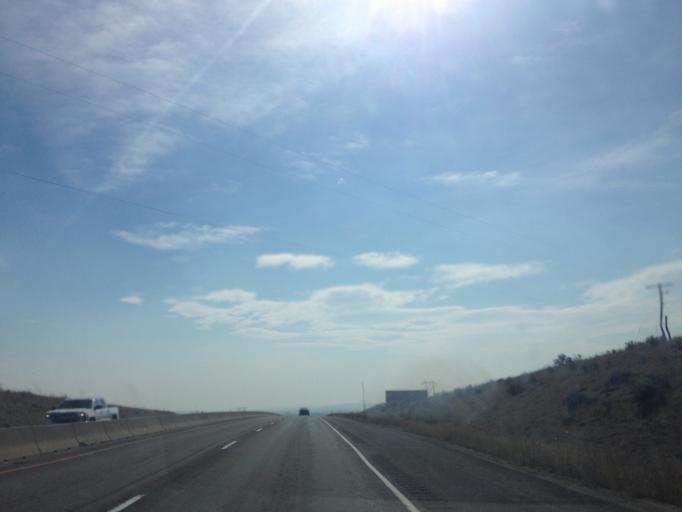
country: US
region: Montana
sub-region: Jefferson County
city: Whitehall
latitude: 45.9111
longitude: -112.2655
